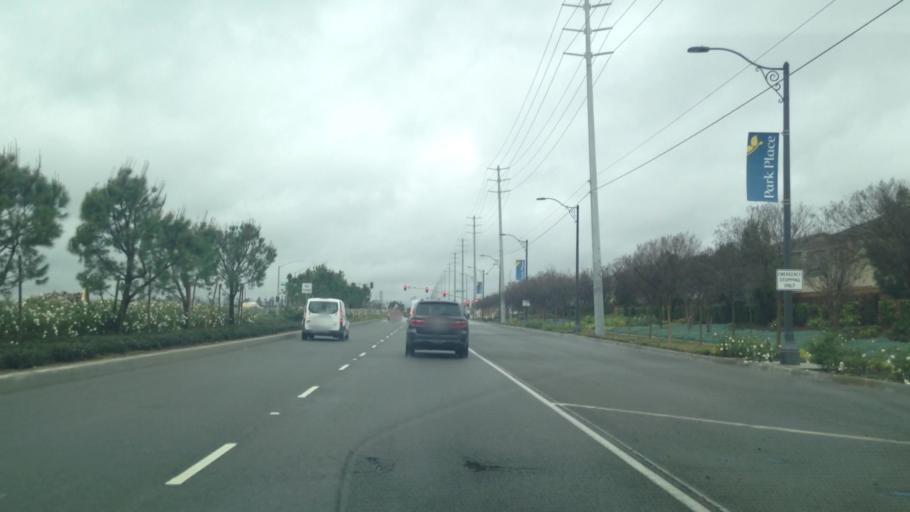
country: US
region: California
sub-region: Riverside County
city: Norco
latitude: 33.9843
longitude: -117.5932
